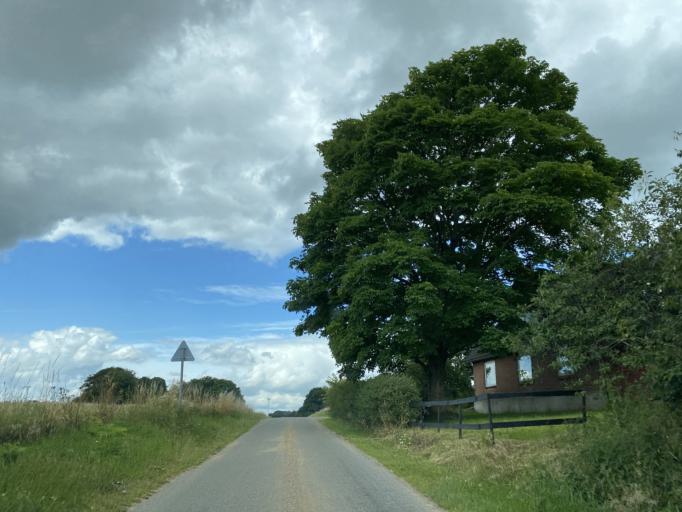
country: DK
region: Central Jutland
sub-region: Silkeborg Kommune
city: Svejbaek
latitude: 56.2364
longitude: 9.6514
